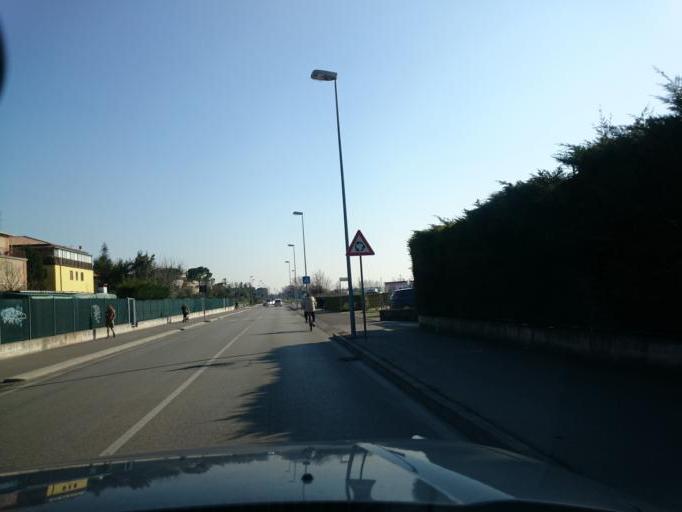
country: IT
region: Veneto
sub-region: Provincia di Padova
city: Mandriola-Sant'Agostino
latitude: 45.3805
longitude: 11.8649
